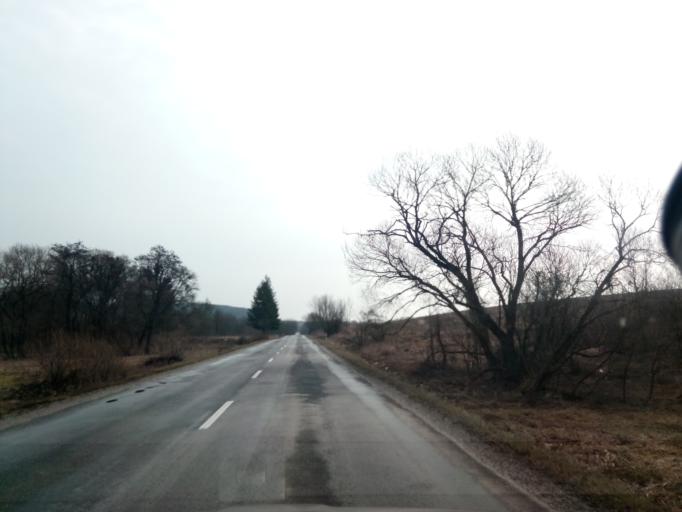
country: SK
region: Kosicky
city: Secovce
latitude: 48.6337
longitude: 21.5106
